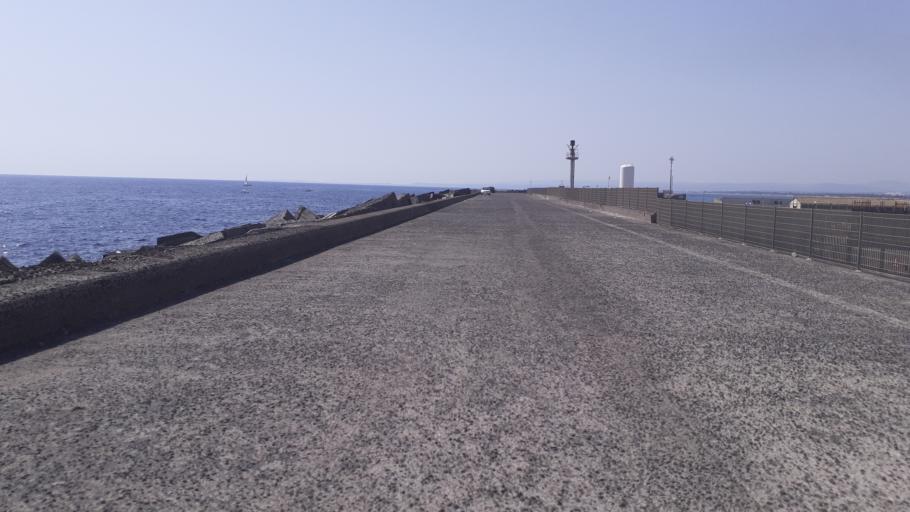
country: IT
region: Sicily
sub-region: Catania
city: Catania
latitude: 37.4933
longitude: 15.0999
